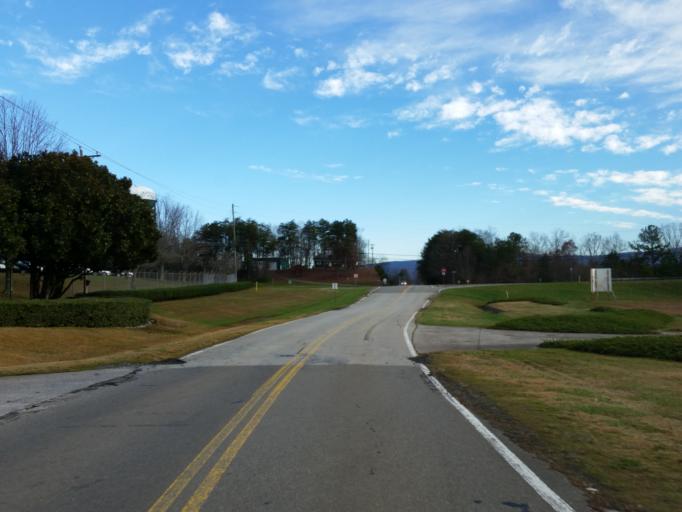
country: US
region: Georgia
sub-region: Pickens County
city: Jasper
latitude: 34.4502
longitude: -84.4521
